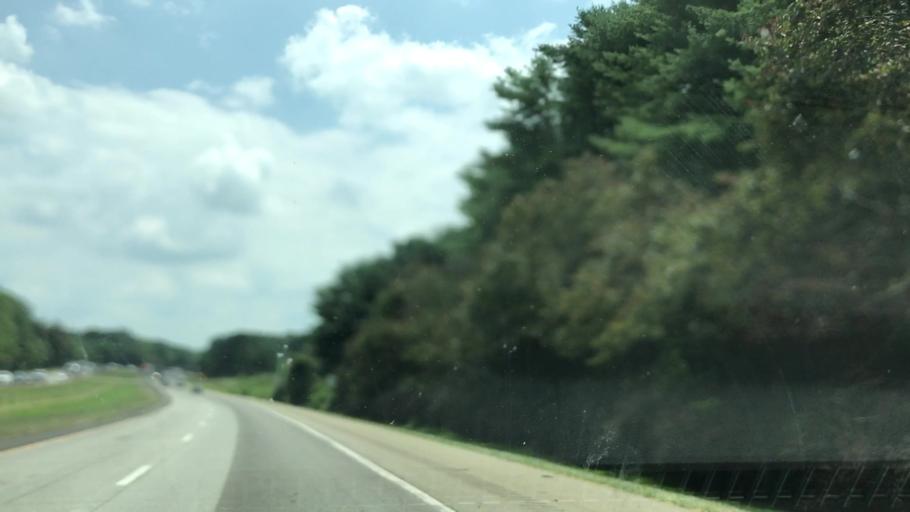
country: US
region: Virginia
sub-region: Carroll County
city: Cana
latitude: 36.5606
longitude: -80.7449
